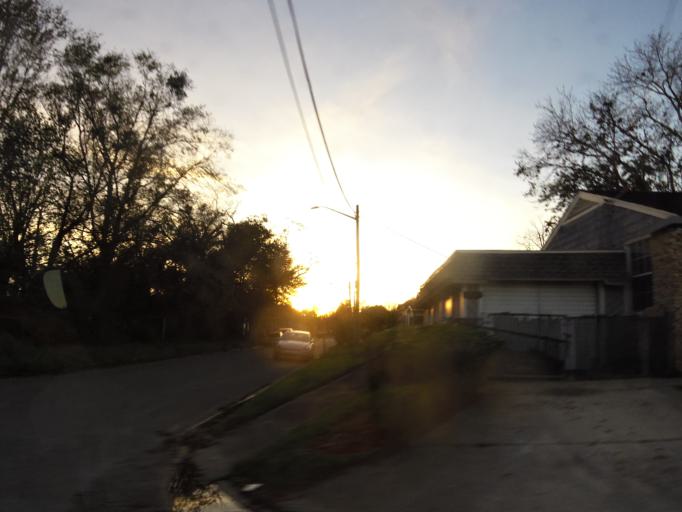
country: US
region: Florida
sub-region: Duval County
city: Jacksonville
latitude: 30.3381
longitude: -81.6972
